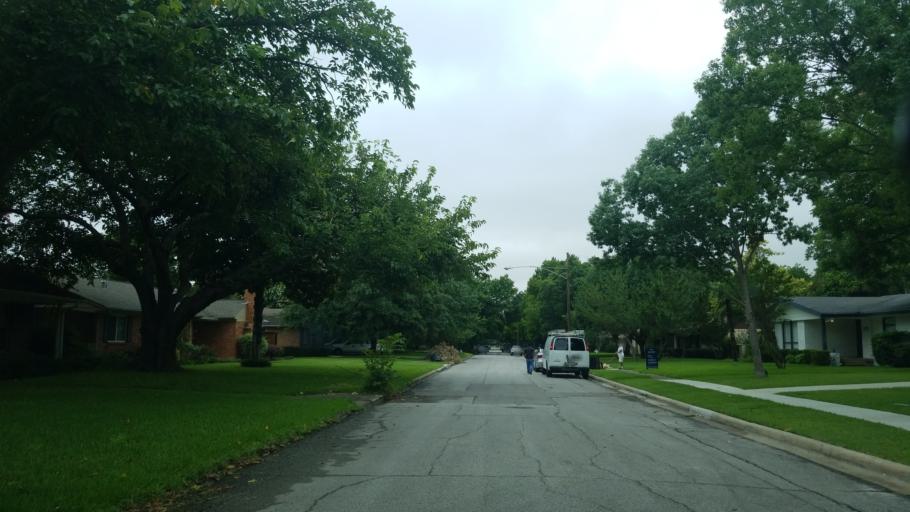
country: US
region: Texas
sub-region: Dallas County
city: Farmers Branch
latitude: 32.8970
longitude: -96.8651
